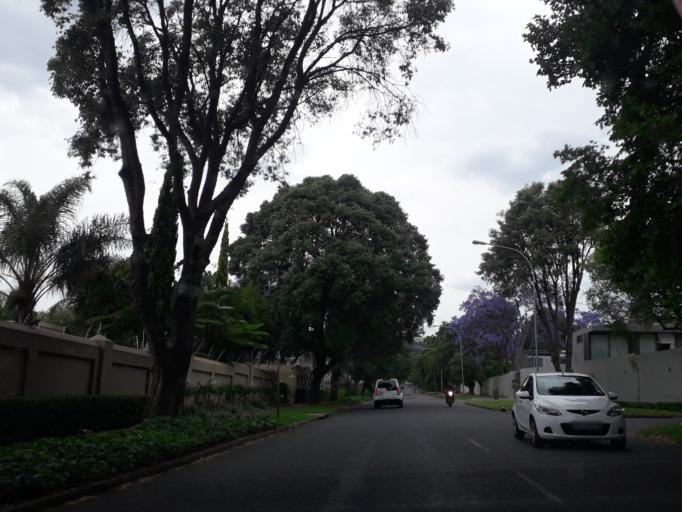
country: ZA
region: Gauteng
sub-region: City of Johannesburg Metropolitan Municipality
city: Johannesburg
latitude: -26.1621
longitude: 28.0652
